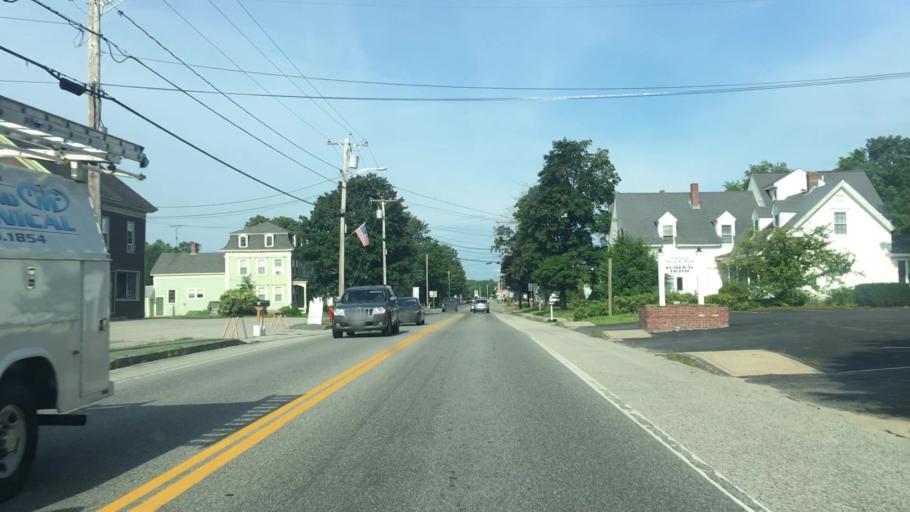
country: US
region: Maine
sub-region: York County
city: Cornish
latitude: 43.8053
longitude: -70.8106
